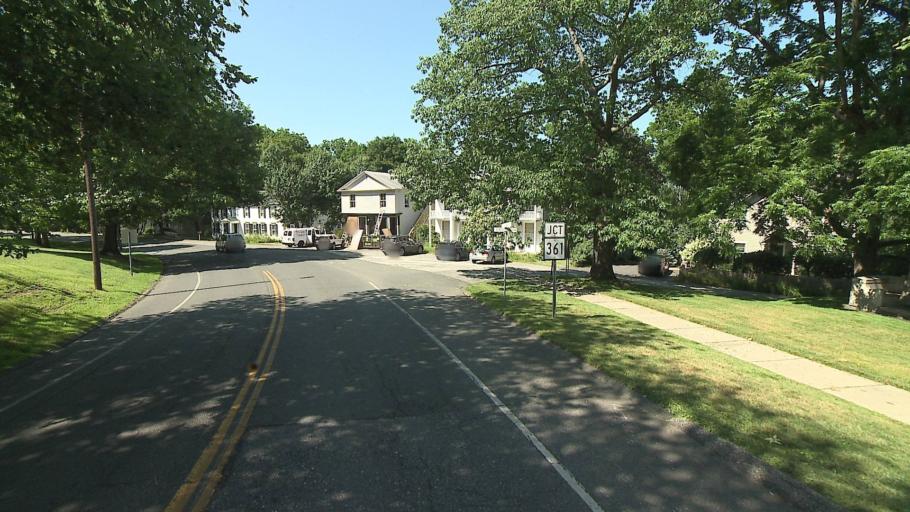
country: US
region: Connecticut
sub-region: Litchfield County
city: Kent
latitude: 41.8816
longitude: -73.4762
